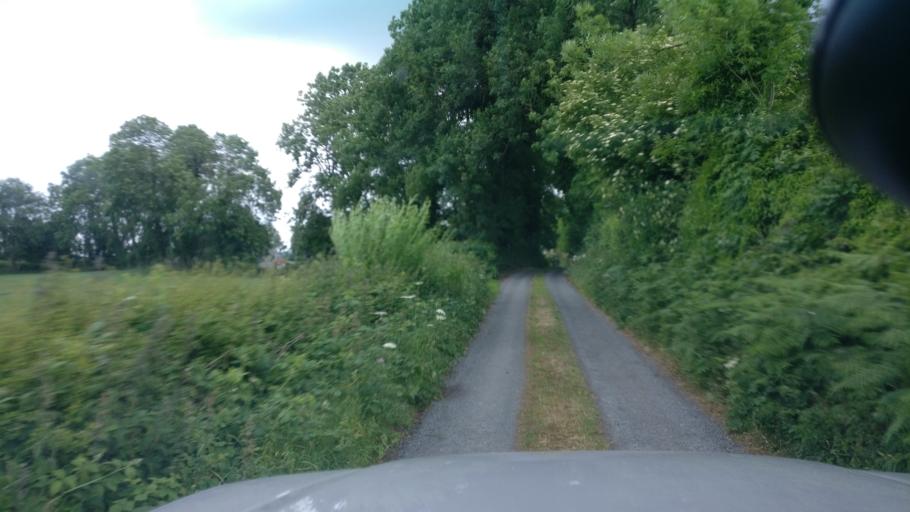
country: IE
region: Connaught
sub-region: County Galway
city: Ballinasloe
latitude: 53.3027
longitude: -8.2871
